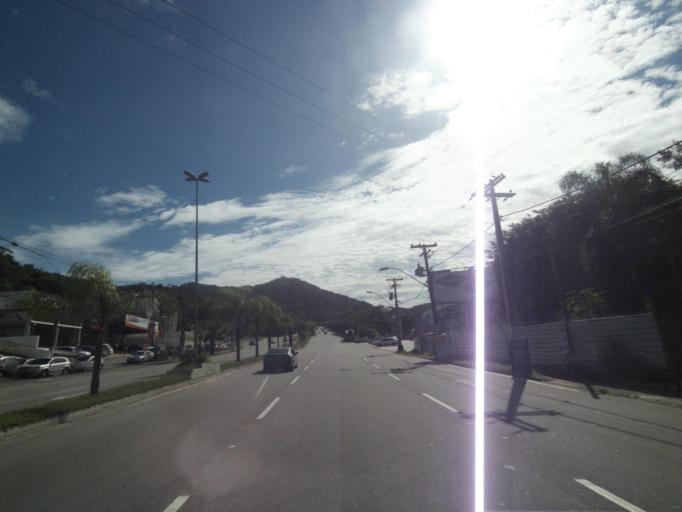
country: BR
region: Rio de Janeiro
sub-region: Niteroi
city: Niteroi
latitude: -22.9285
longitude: -43.0637
